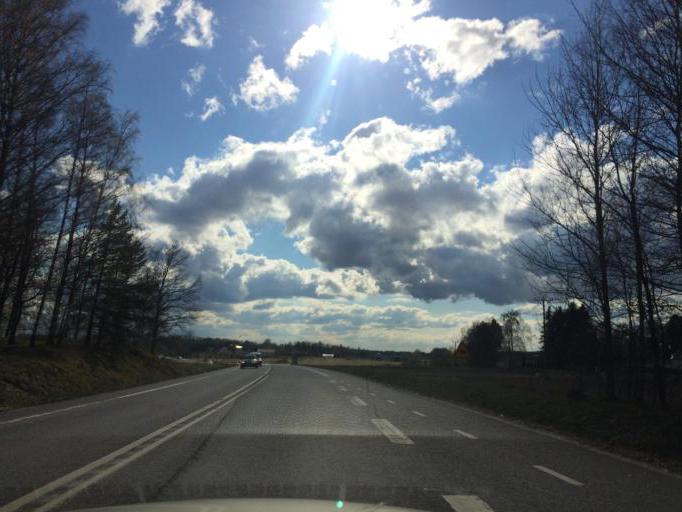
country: SE
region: Soedermanland
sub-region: Eskilstuna Kommun
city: Eskilstuna
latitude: 59.4309
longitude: 16.6168
